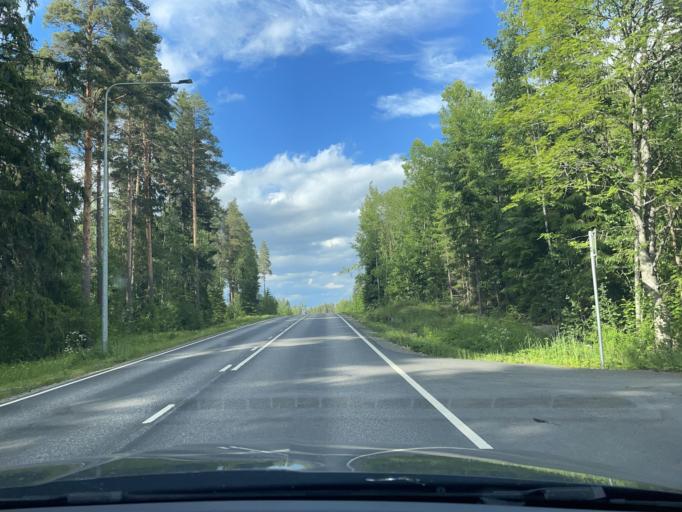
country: FI
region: Central Finland
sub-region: Jaemsae
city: Jaemsaenkoski
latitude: 62.0843
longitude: 25.1449
